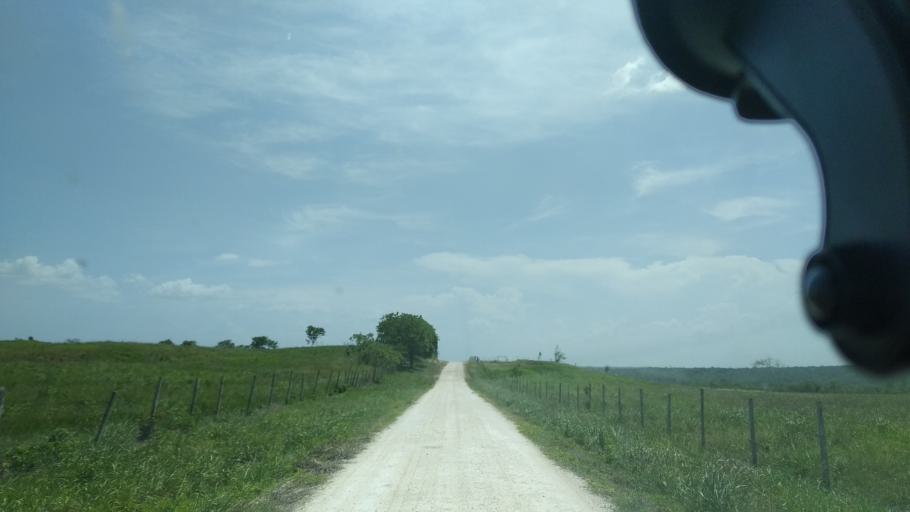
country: BZ
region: Cayo
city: San Ignacio
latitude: 17.2913
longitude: -89.0732
